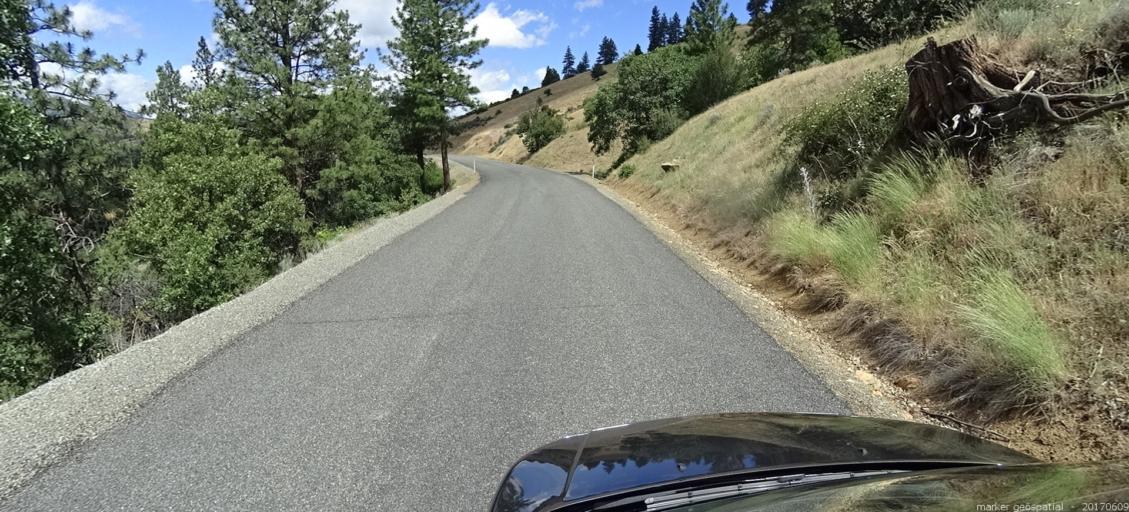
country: US
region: California
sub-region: Siskiyou County
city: Weed
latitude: 41.3269
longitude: -122.8097
